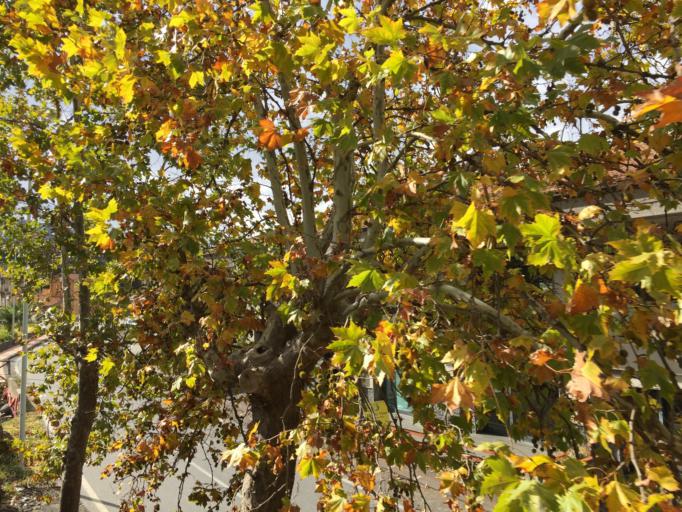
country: IT
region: Sicily
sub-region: Messina
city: Moio Alcantara
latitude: 37.8717
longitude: 15.0397
